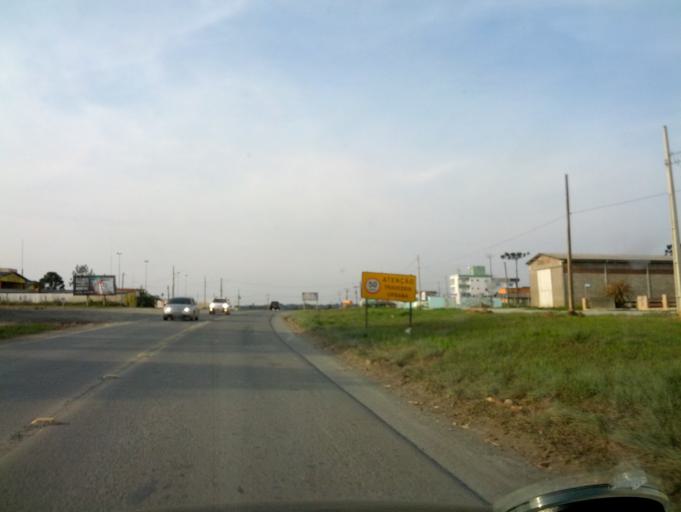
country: BR
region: Santa Catarina
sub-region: Otacilio Costa
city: Otacilio Costa
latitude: -27.5037
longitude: -50.1272
